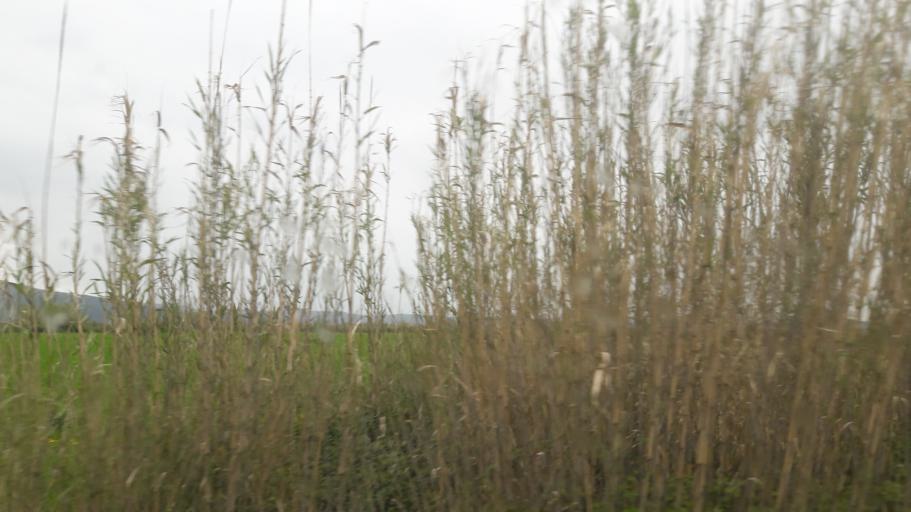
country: AL
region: Shkoder
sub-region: Rrethi i Shkodres
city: Berdica e Madhe
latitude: 41.9626
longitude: 19.5026
